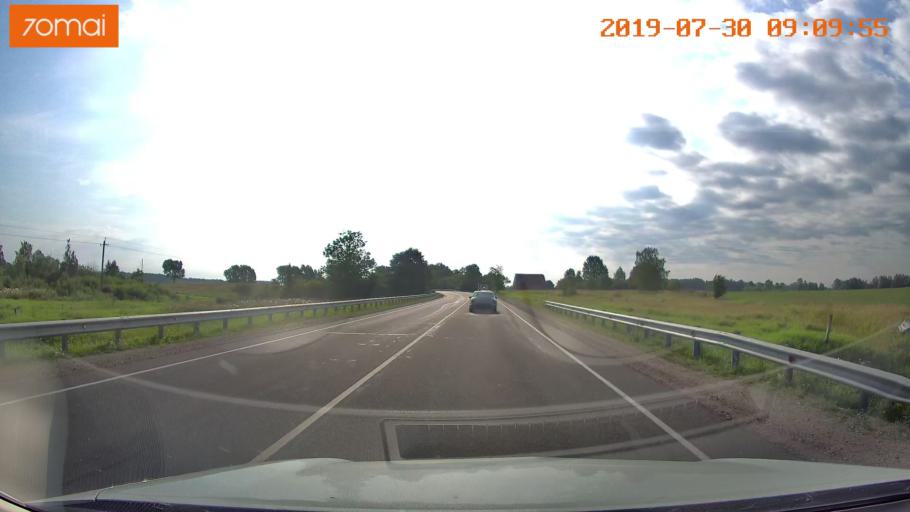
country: RU
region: Kaliningrad
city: Nesterov
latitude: 54.6122
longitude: 22.4174
